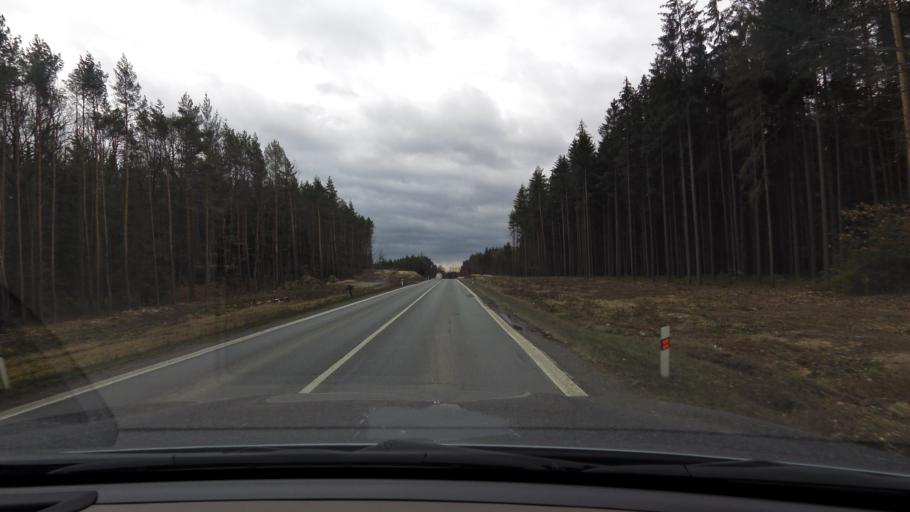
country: CZ
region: Plzensky
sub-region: Okres Plzen-Sever
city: Tremosna
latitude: 49.7989
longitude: 13.3870
